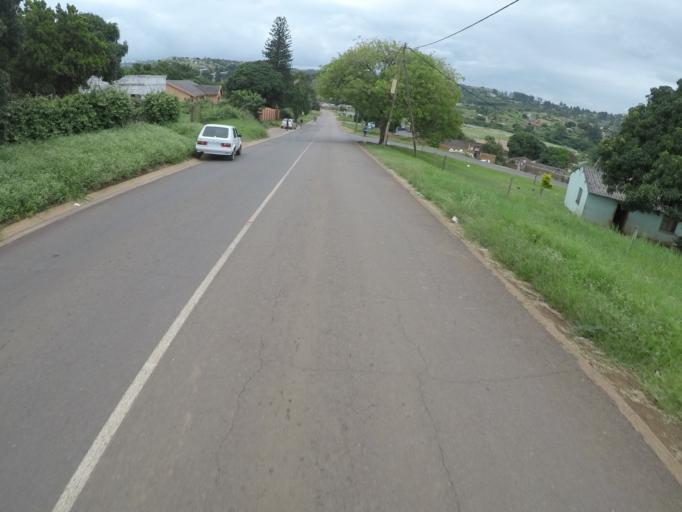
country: ZA
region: KwaZulu-Natal
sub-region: uThungulu District Municipality
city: Empangeni
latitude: -28.7680
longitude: 31.8642
